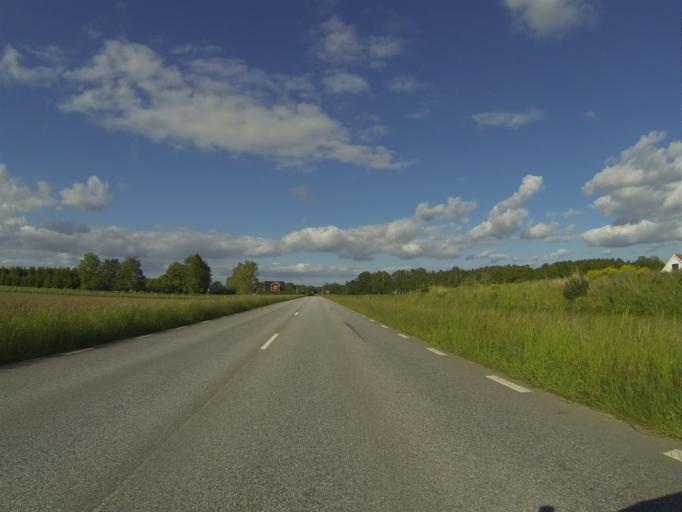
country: SE
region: Skane
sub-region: Lunds Kommun
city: Genarp
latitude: 55.7283
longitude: 13.3781
